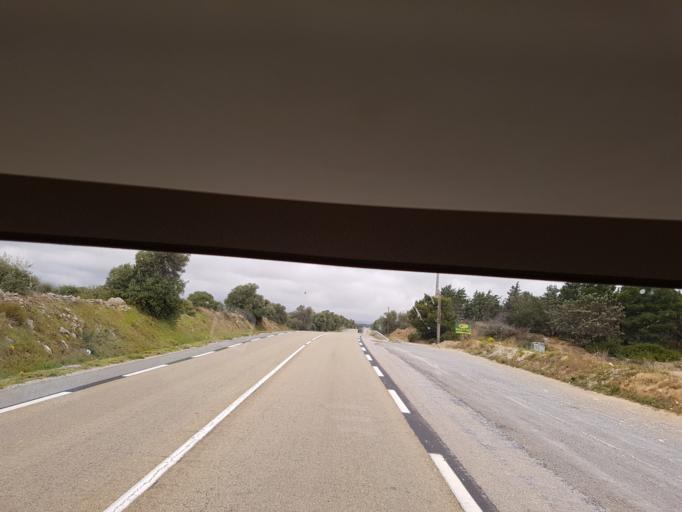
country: FR
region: Languedoc-Roussillon
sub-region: Departement de l'Aude
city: Leucate
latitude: 42.9056
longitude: 3.0002
